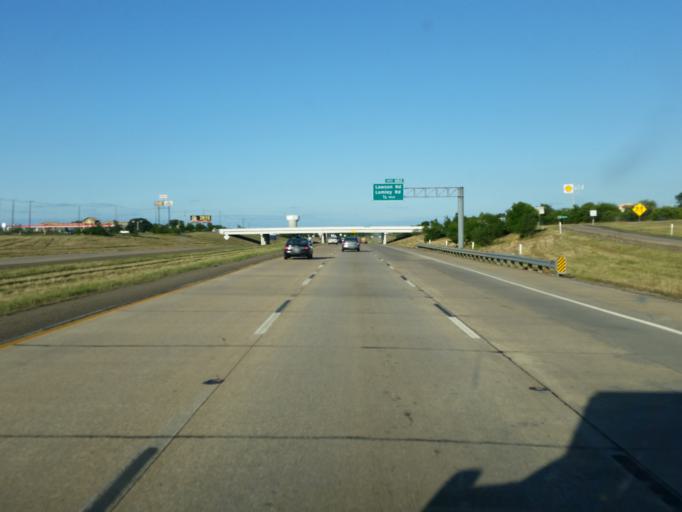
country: US
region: Texas
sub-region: Dallas County
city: Balch Springs
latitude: 32.7038
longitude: -96.5901
